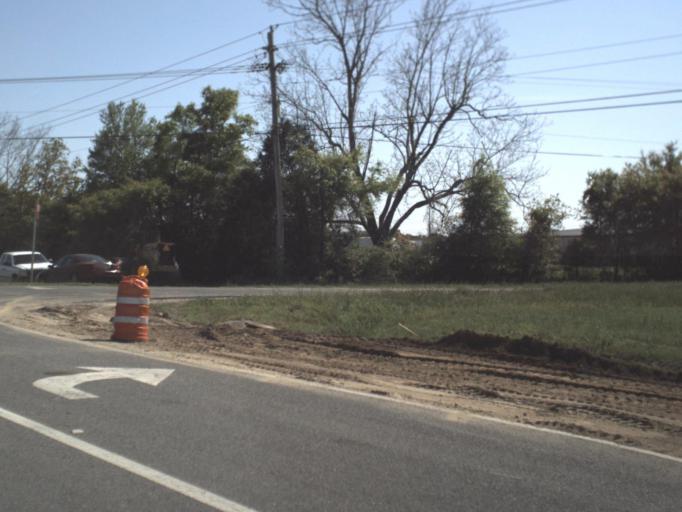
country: US
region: Florida
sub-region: Escambia County
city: Bellview
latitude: 30.4761
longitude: -87.3084
